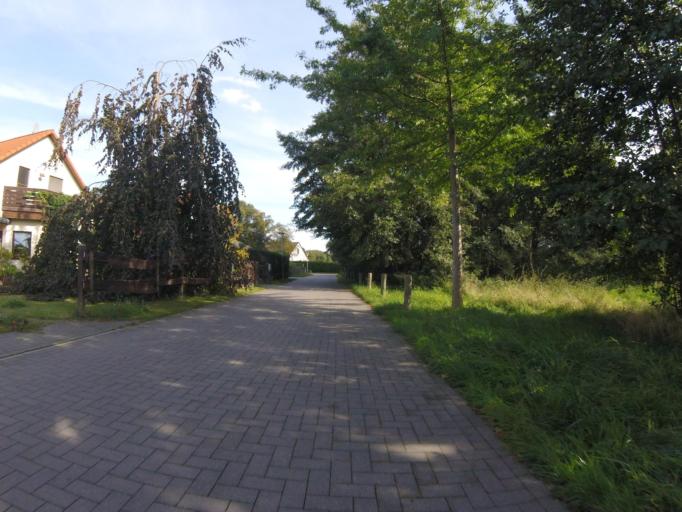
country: DE
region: Brandenburg
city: Bestensee
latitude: 52.2959
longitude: 13.7194
